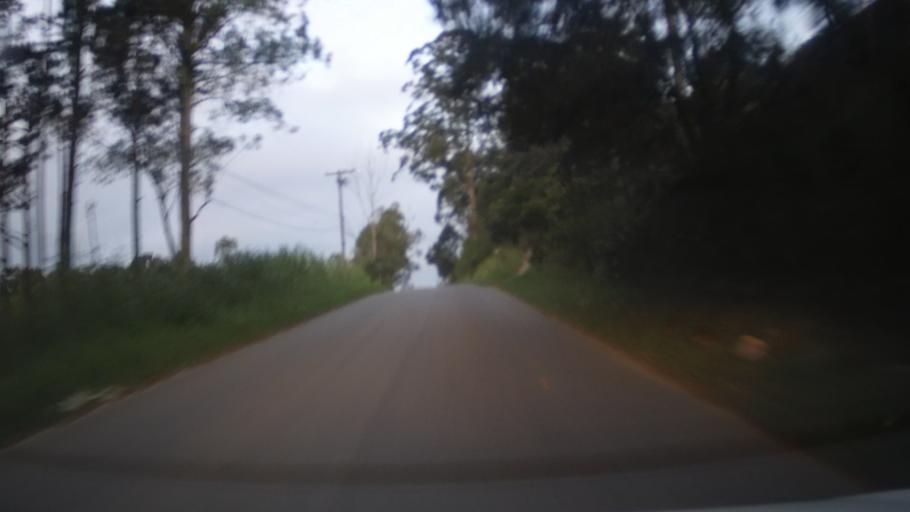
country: BR
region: Sao Paulo
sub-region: Aruja
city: Aruja
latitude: -23.3731
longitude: -46.2990
